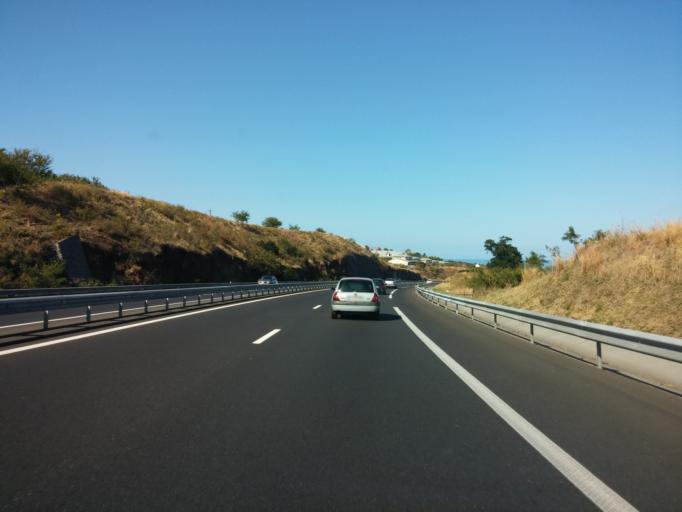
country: RE
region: Reunion
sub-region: Reunion
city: Saint-Leu
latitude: -21.1952
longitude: 55.2962
